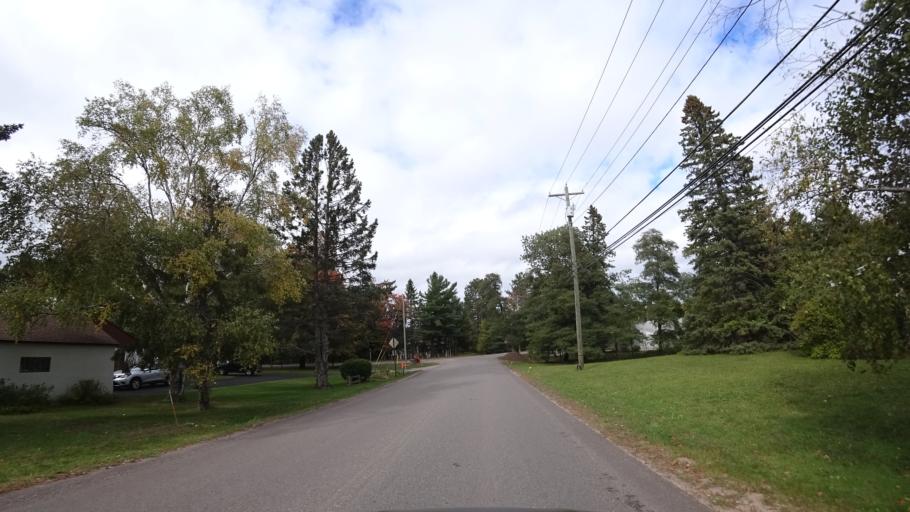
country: US
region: Michigan
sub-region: Marquette County
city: Trowbridge Park
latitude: 46.5470
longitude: -87.4374
